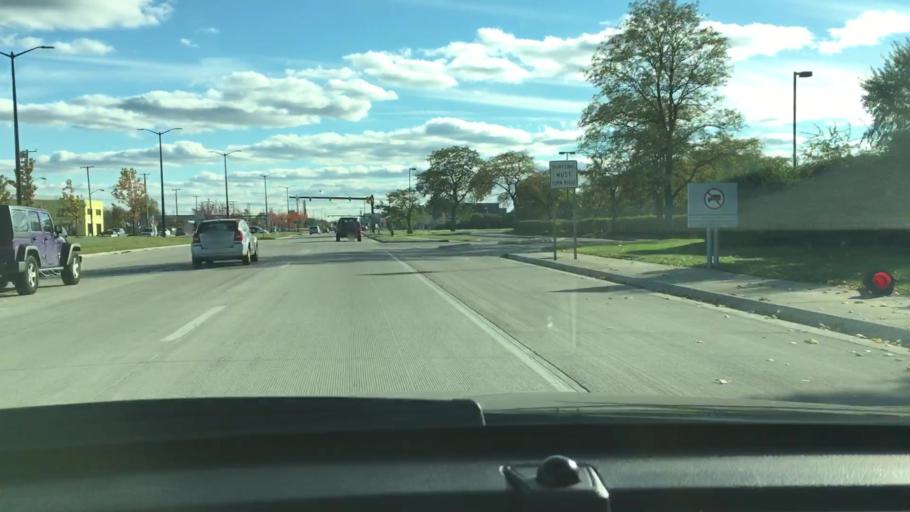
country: US
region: Michigan
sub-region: Macomb County
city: Sterling Heights
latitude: 42.5544
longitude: -83.0294
